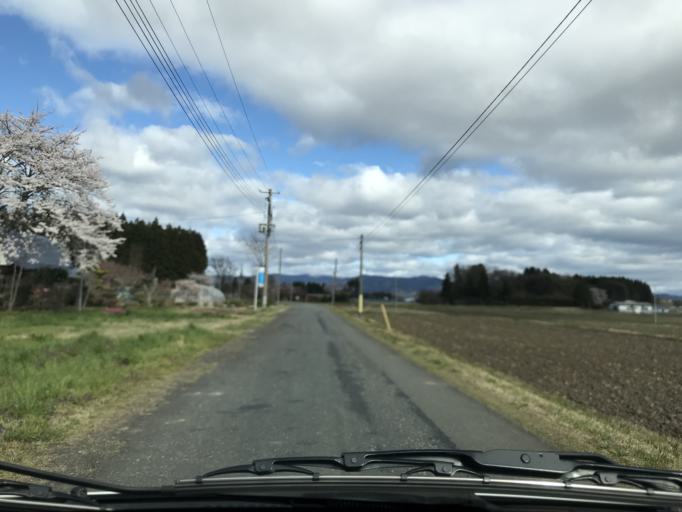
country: JP
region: Iwate
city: Mizusawa
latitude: 39.1124
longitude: 141.1071
